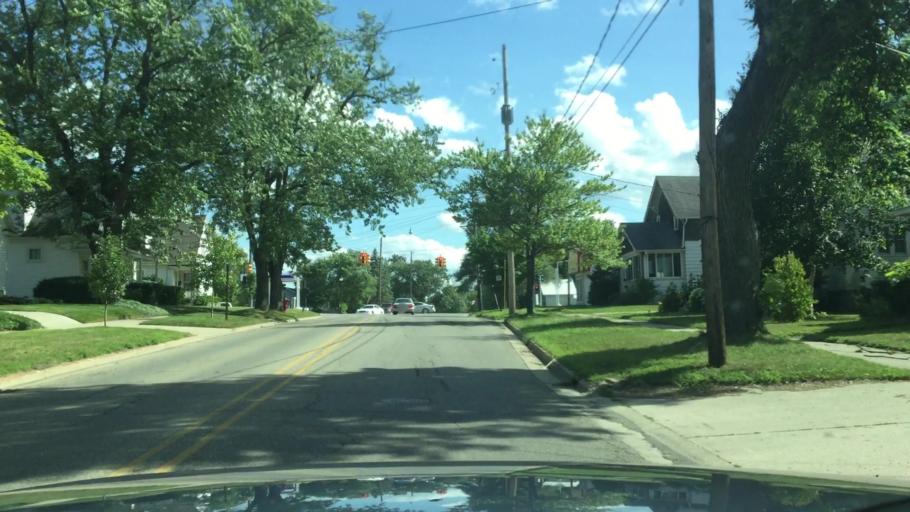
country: US
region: Michigan
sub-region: Ionia County
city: Belding
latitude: 43.0898
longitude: -85.2288
